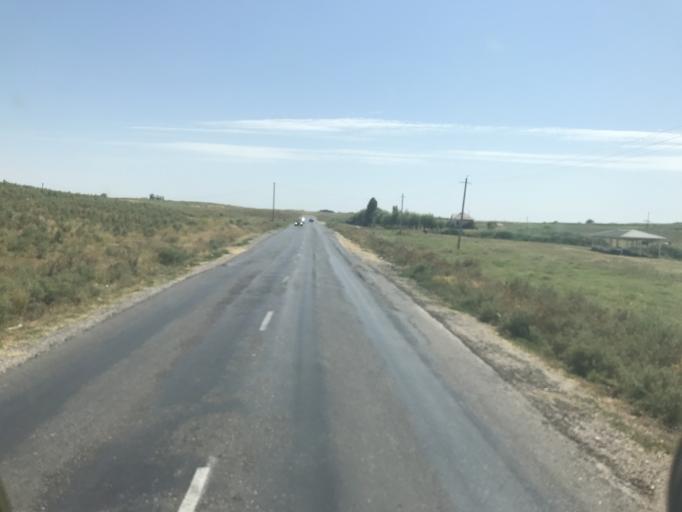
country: UZ
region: Toshkent
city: Yangiyul
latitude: 41.3552
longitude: 68.8619
